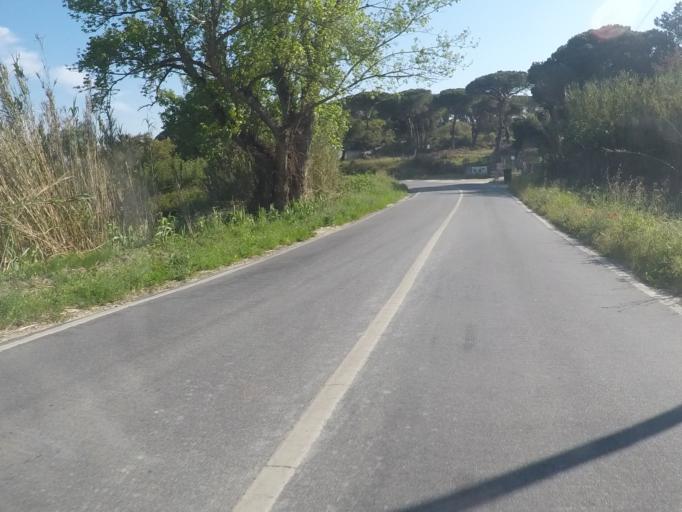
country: PT
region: Setubal
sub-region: Sesimbra
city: Sesimbra
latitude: 38.5038
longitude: -9.1486
